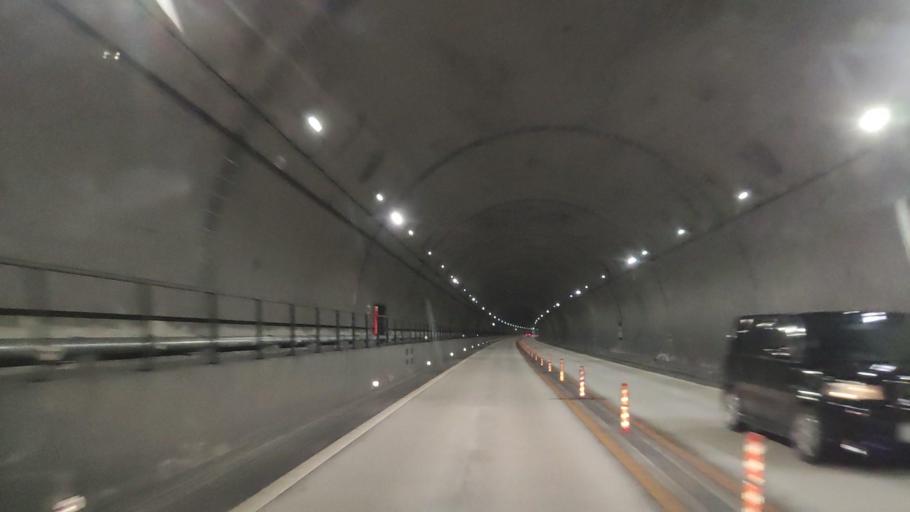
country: JP
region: Ehime
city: Hojo
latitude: 34.0790
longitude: 132.9762
